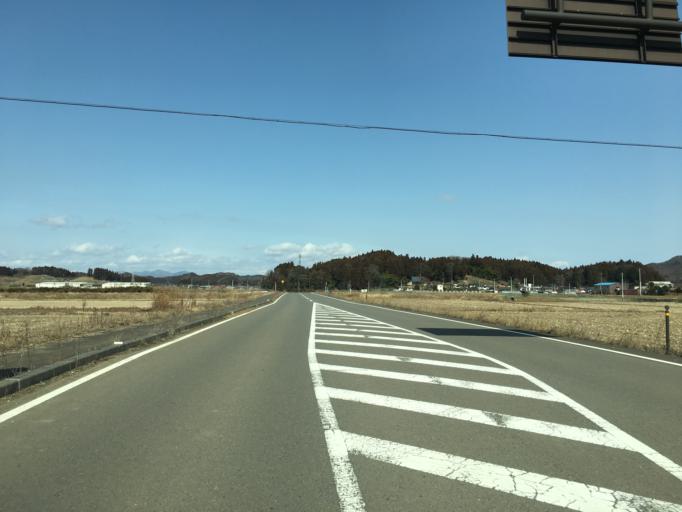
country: JP
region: Fukushima
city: Ishikawa
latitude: 37.1164
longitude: 140.2776
